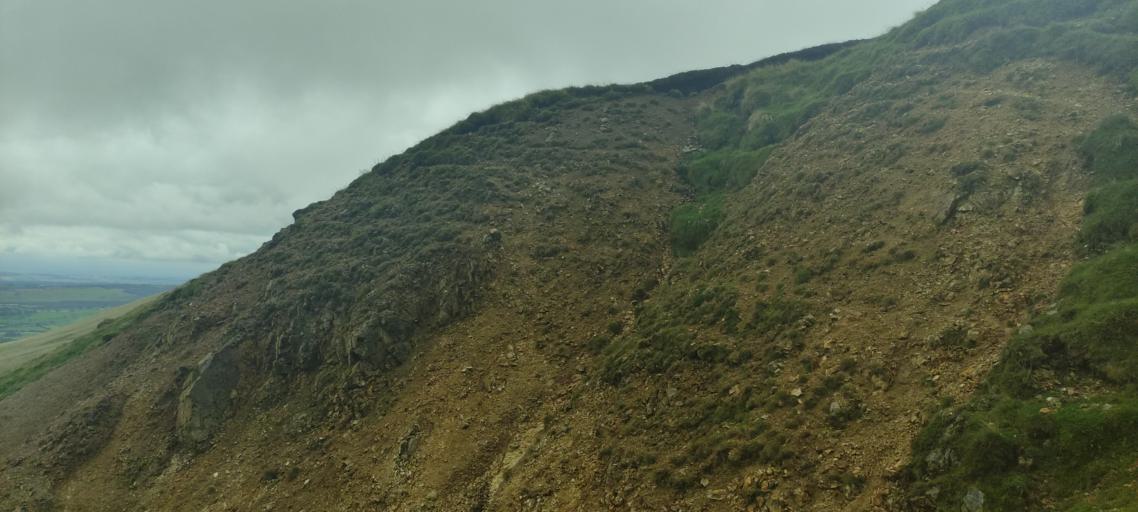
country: GB
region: England
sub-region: Cumbria
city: Keswick
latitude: 54.7011
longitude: -3.0560
